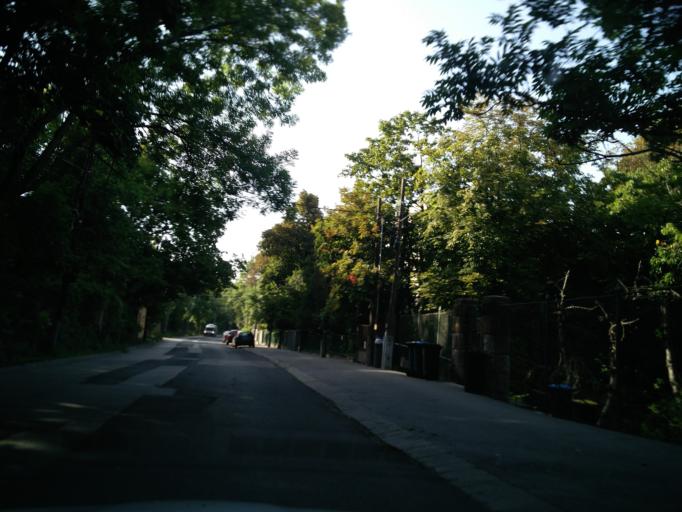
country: HU
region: Budapest
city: Budapest XII. keruelet
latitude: 47.5036
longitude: 18.9841
